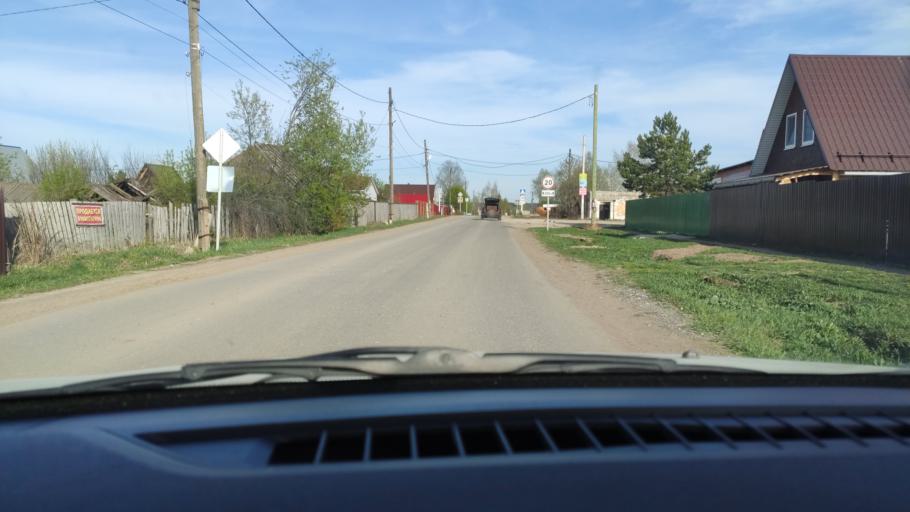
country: RU
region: Perm
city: Sylva
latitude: 57.9306
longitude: 56.6919
